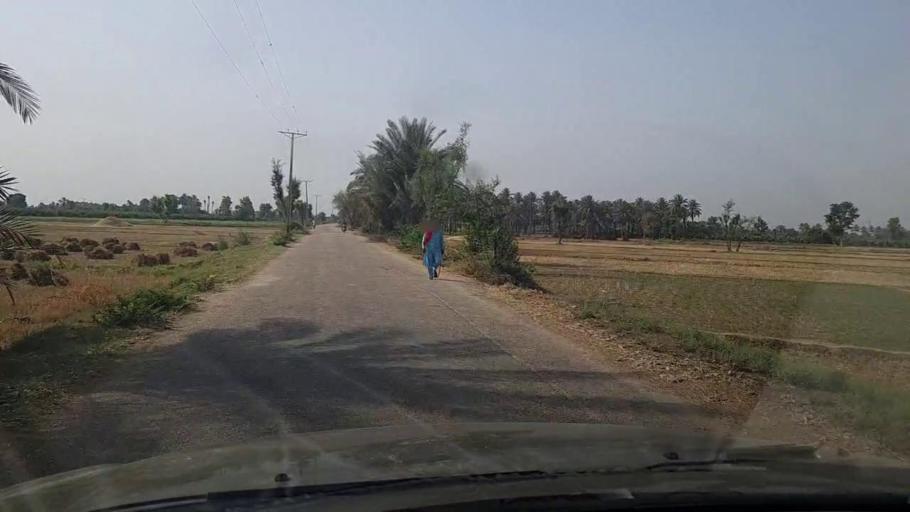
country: PK
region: Sindh
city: Kot Diji
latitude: 27.2779
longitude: 68.6510
